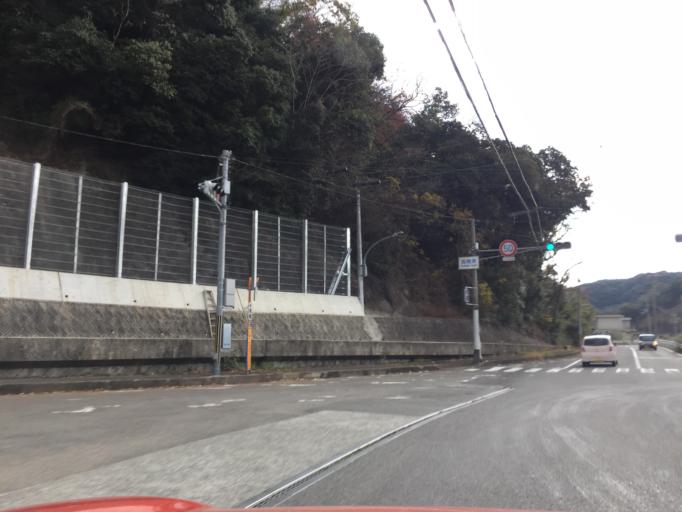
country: JP
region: Wakayama
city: Kainan
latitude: 34.1660
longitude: 135.2517
